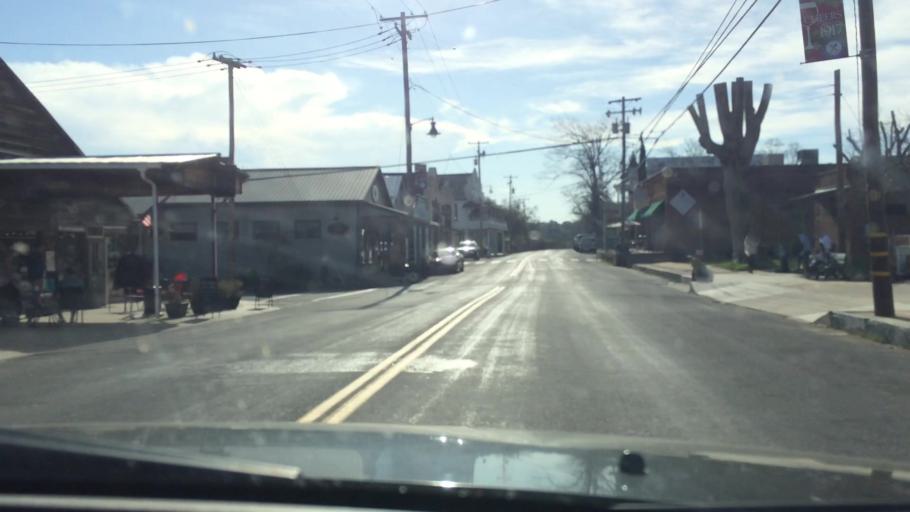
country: US
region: California
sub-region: Amador County
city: Plymouth
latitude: 38.4812
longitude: -120.8475
